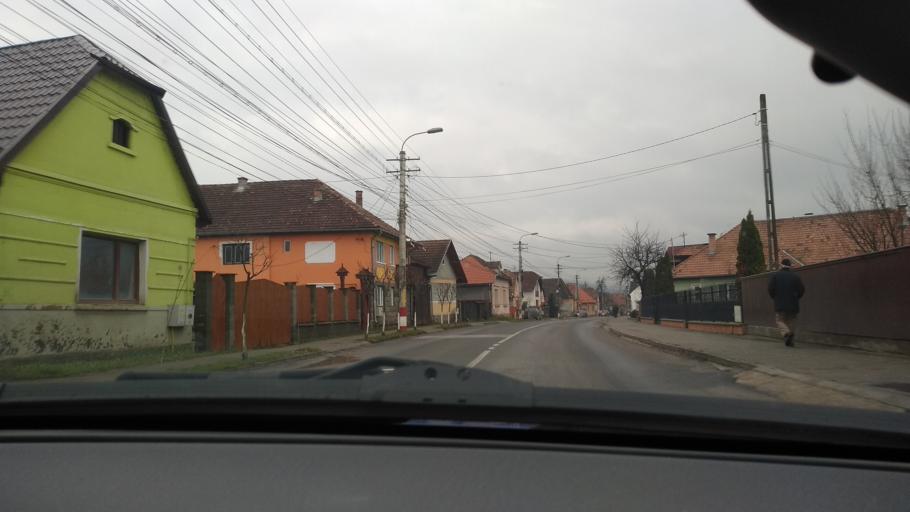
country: RO
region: Mures
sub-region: Oras Sovata
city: Sovata
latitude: 46.5880
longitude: 25.0669
